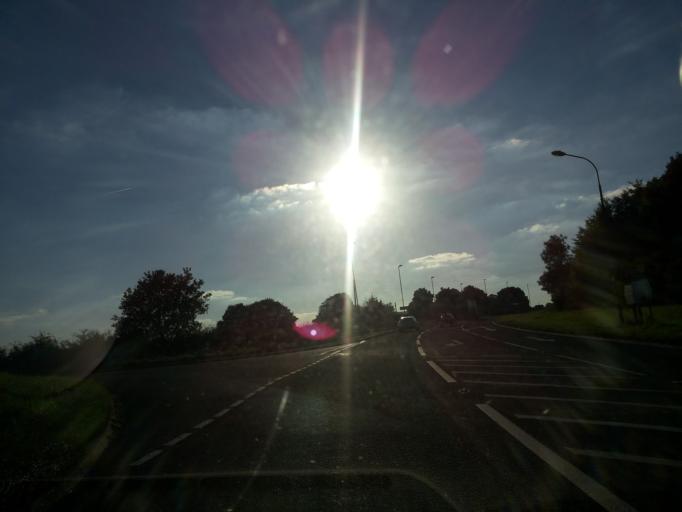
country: GB
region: England
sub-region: Derbyshire
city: Tibshelf
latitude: 53.1942
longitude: -1.3303
